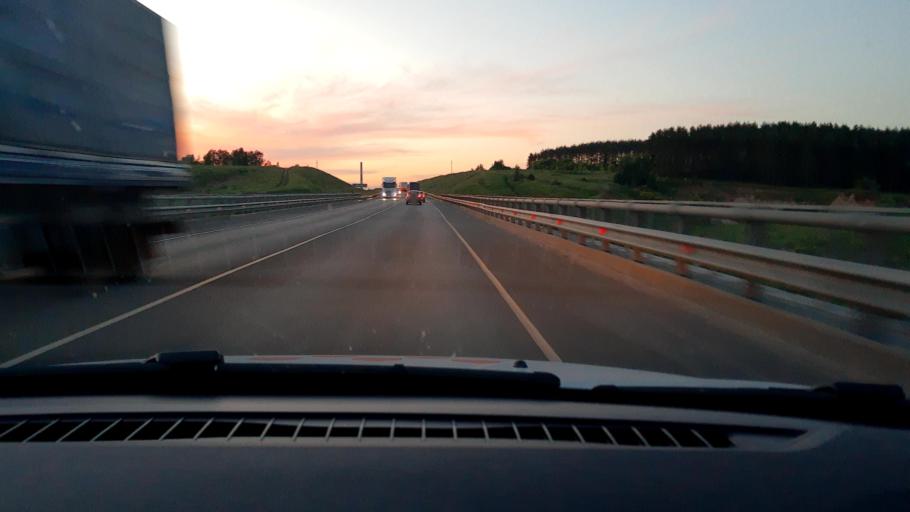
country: RU
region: Nizjnij Novgorod
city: Kstovo
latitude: 56.0787
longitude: 44.1341
